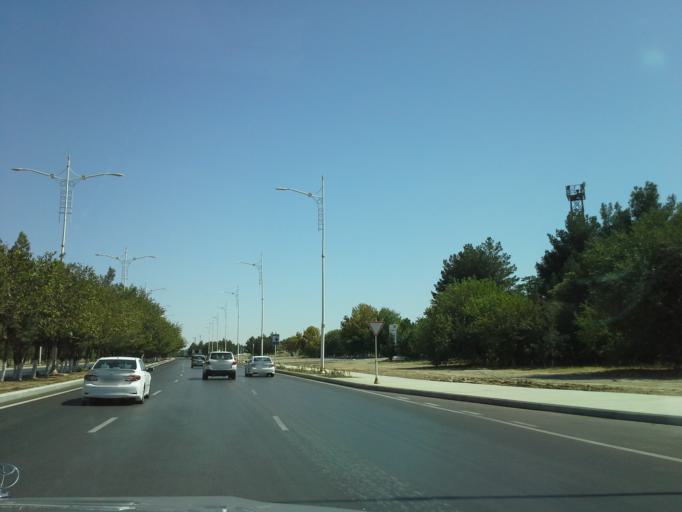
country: TM
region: Ahal
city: Ashgabat
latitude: 37.9221
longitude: 58.4424
